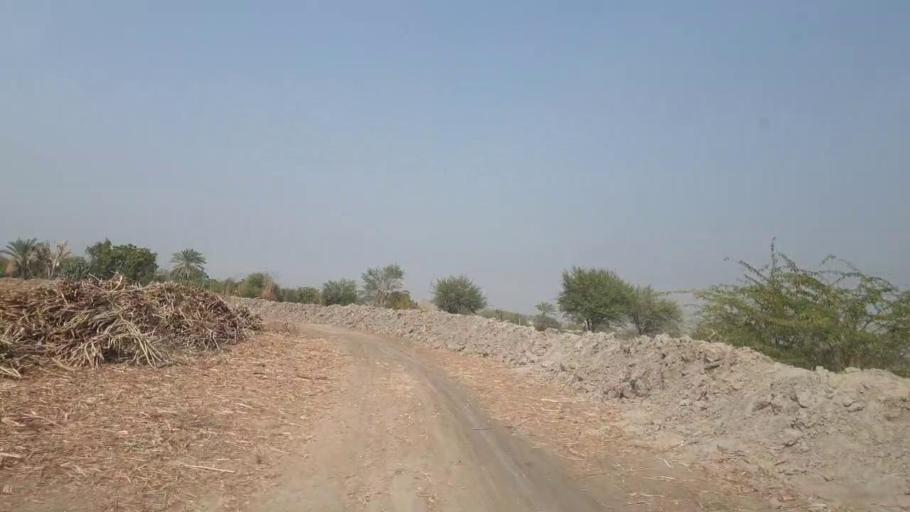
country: PK
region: Sindh
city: Mirpur Khas
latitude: 25.5667
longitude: 69.1431
